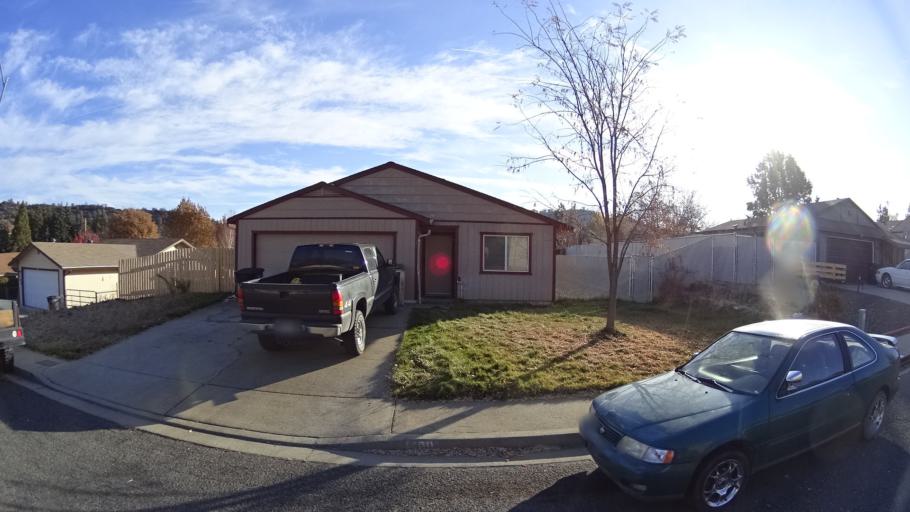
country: US
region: California
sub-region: Siskiyou County
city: Yreka
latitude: 41.7104
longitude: -122.6224
